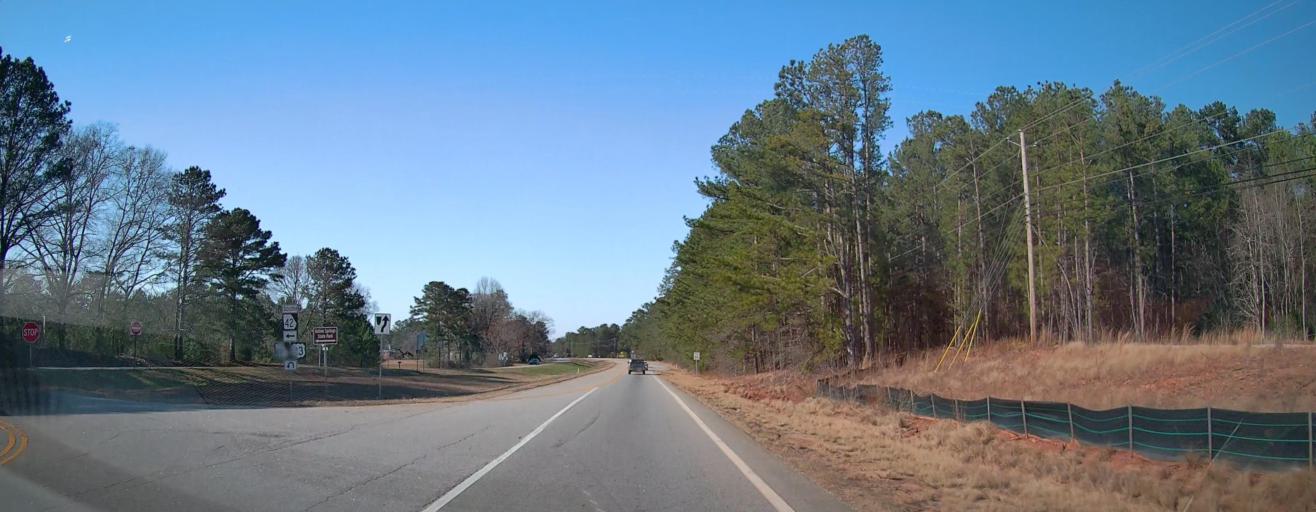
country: US
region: Georgia
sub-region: Butts County
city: Indian Springs
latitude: 33.2647
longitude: -83.9090
